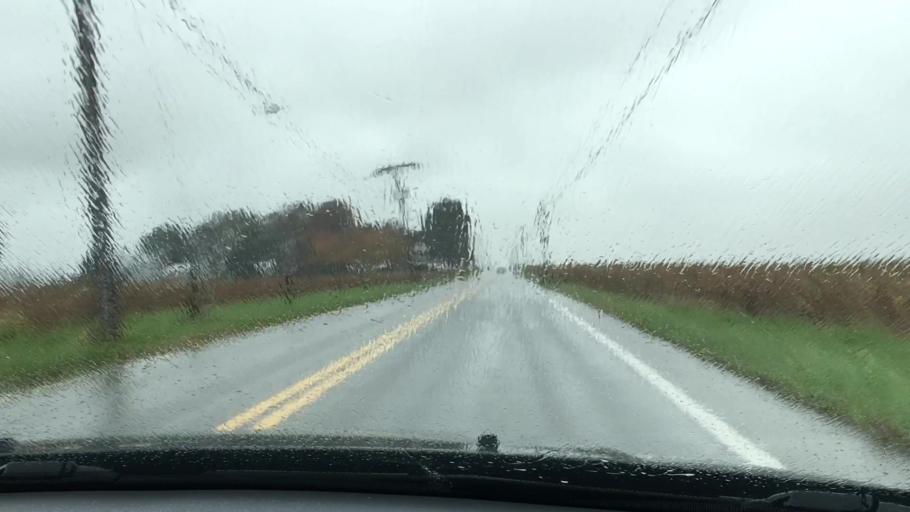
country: US
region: Maryland
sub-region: Frederick County
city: Buckeystown
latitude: 39.3129
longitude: -77.4424
